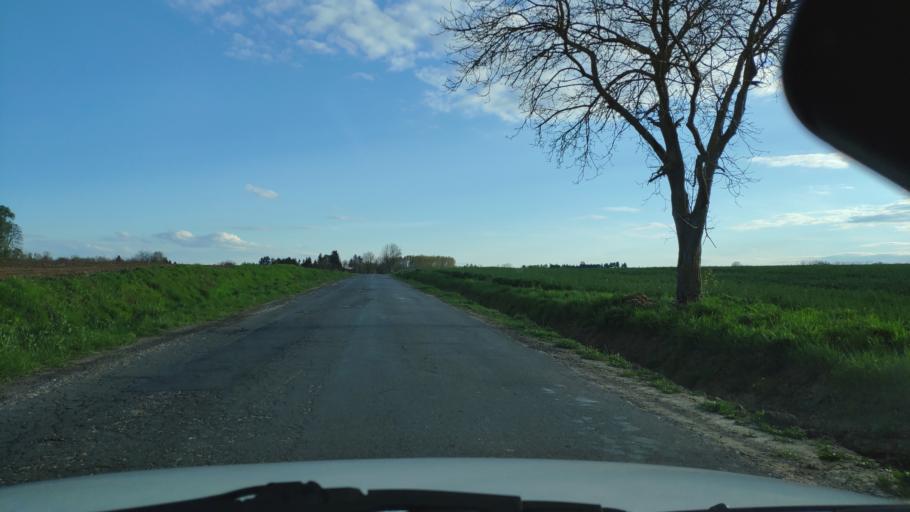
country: HU
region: Zala
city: Zalakomar
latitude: 46.4628
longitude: 17.1259
